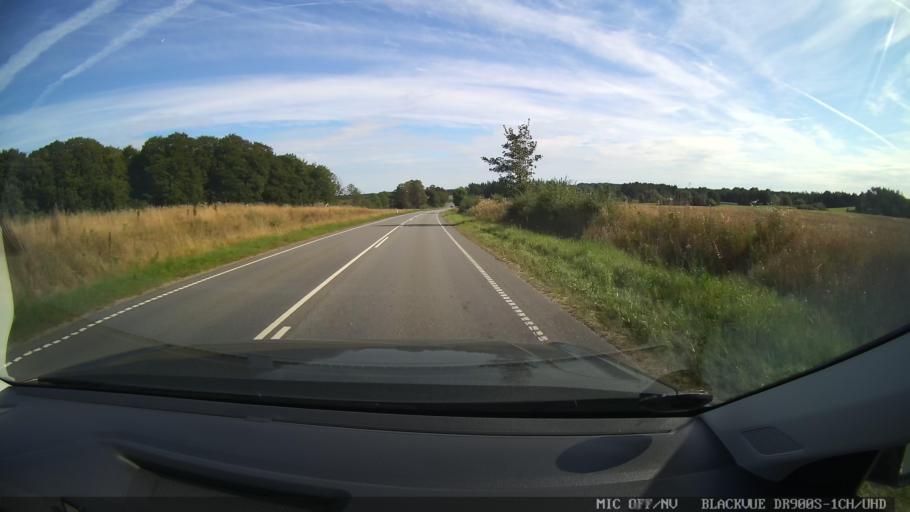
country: DK
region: North Denmark
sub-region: Mariagerfjord Kommune
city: Hadsund
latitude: 56.7933
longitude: 10.0296
